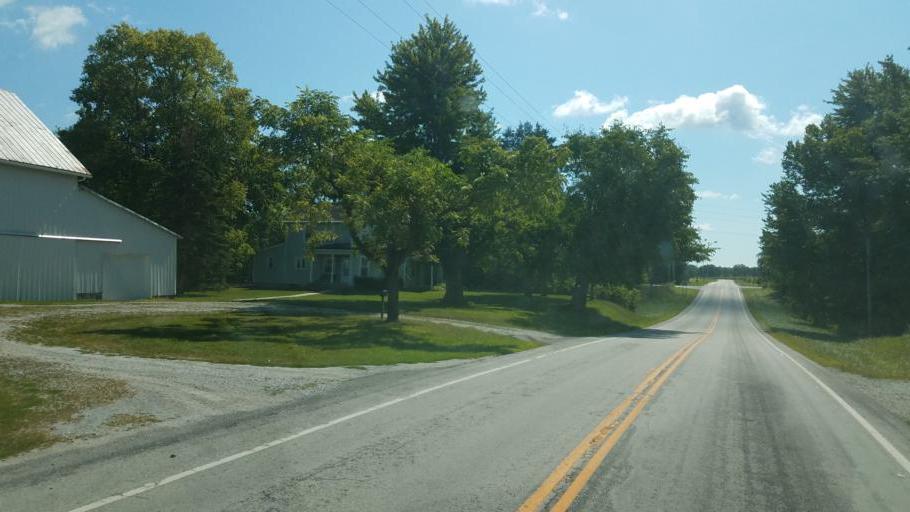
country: US
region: Ohio
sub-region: Wyandot County
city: Carey
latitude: 40.9447
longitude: -83.3210
